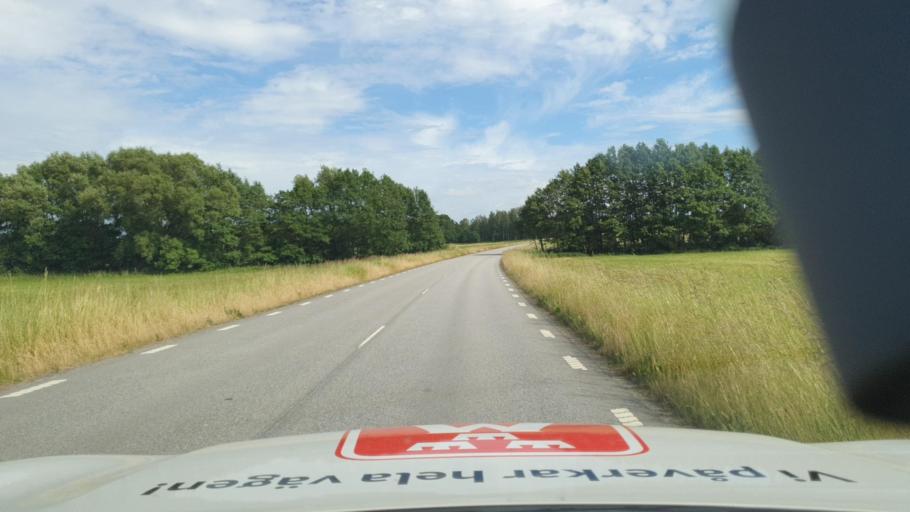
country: SE
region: Skane
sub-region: Sjobo Kommun
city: Blentarp
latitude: 55.5998
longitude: 13.5938
